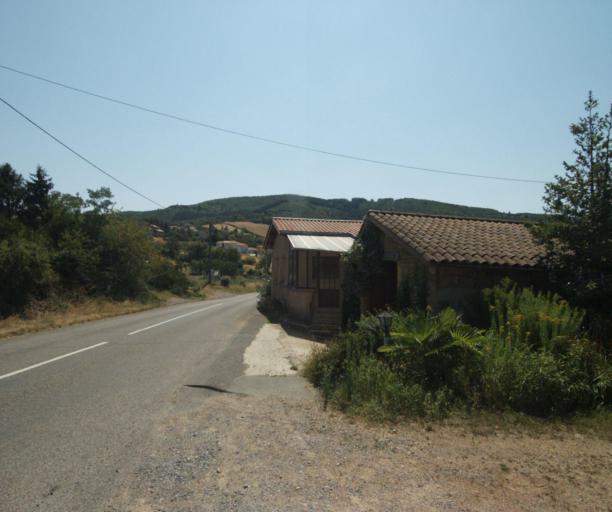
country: FR
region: Rhone-Alpes
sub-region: Departement du Rhone
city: Saint-Pierre-la-Palud
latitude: 45.7847
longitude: 4.6193
